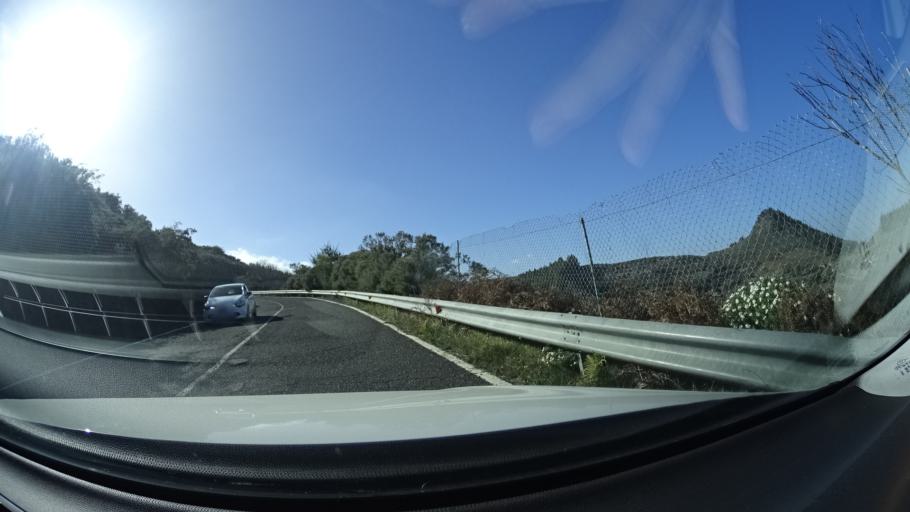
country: ES
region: Canary Islands
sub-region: Provincia de Las Palmas
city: Vega de San Mateo
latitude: 27.9646
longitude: -15.5482
